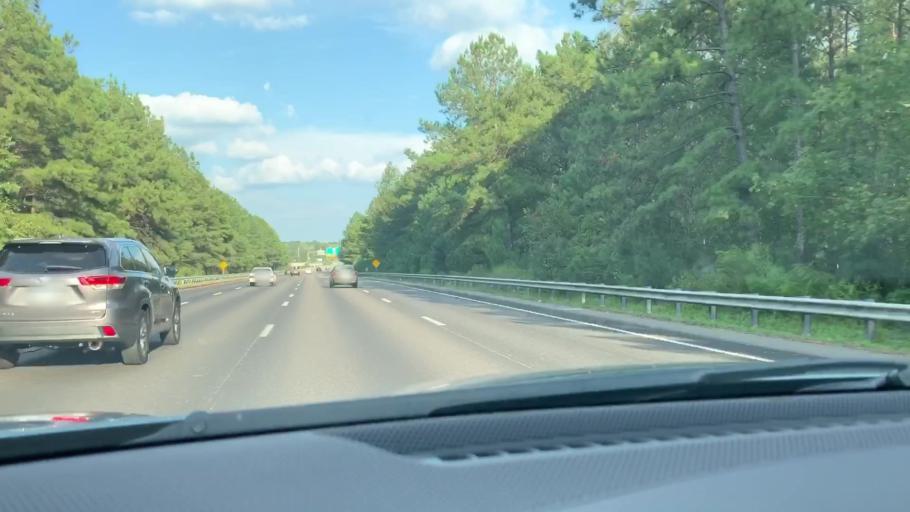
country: US
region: South Carolina
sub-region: Lexington County
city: Cayce
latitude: 33.9290
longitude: -81.0554
